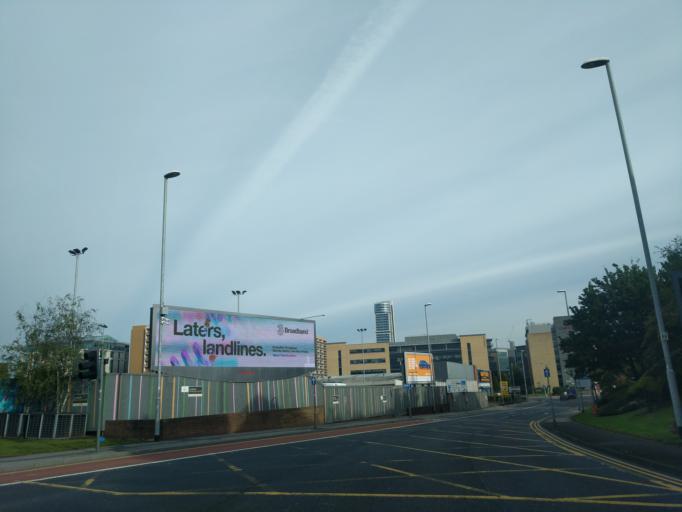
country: GB
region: England
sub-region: City and Borough of Leeds
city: Leeds
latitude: 53.7864
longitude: -1.5480
